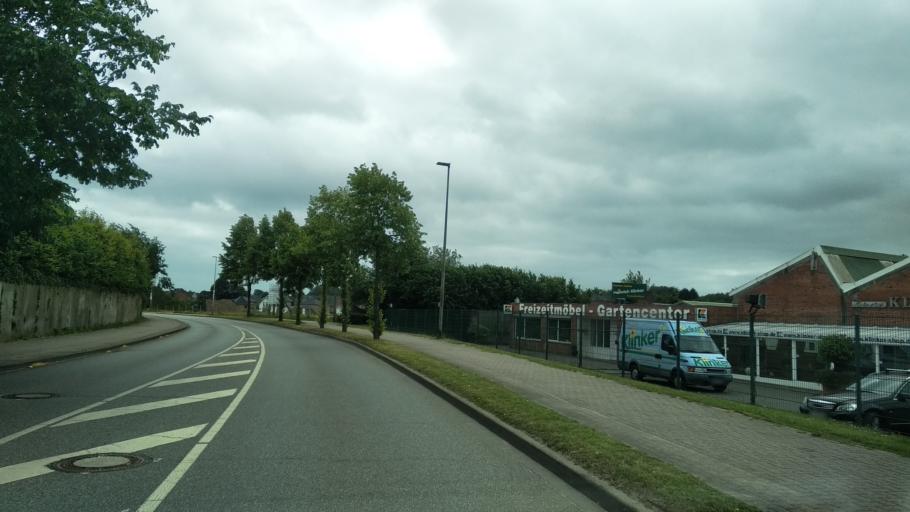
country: DE
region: Schleswig-Holstein
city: Schleswig
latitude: 54.5328
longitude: 9.5565
